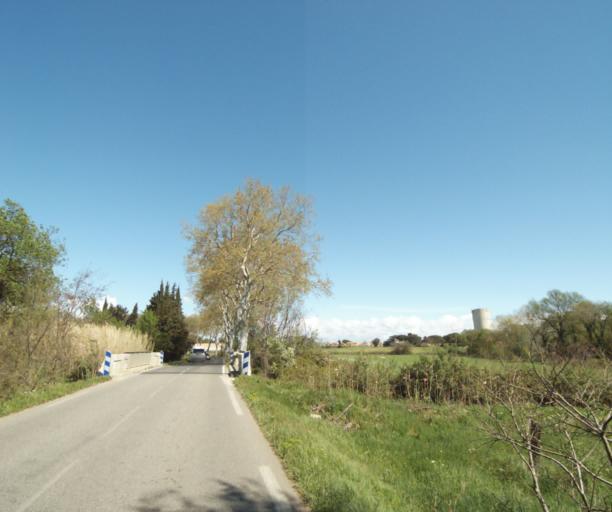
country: FR
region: Languedoc-Roussillon
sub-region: Departement de l'Herault
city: Villeneuve-les-Maguelone
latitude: 43.5604
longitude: 3.8662
